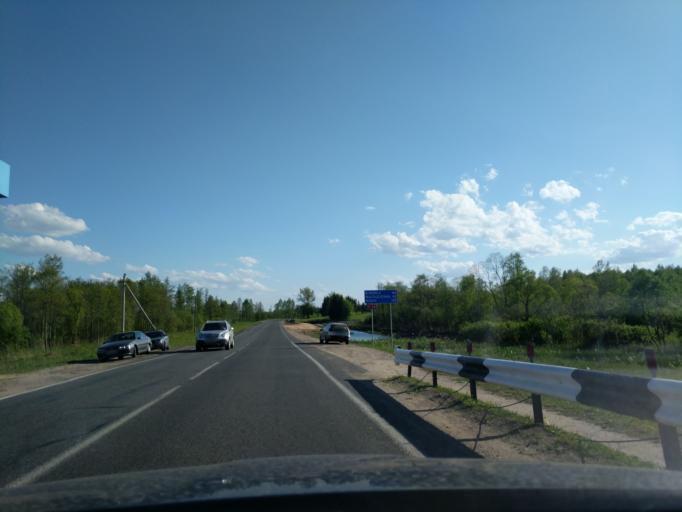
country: BY
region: Minsk
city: Myadzyel
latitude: 54.8640
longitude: 26.9331
